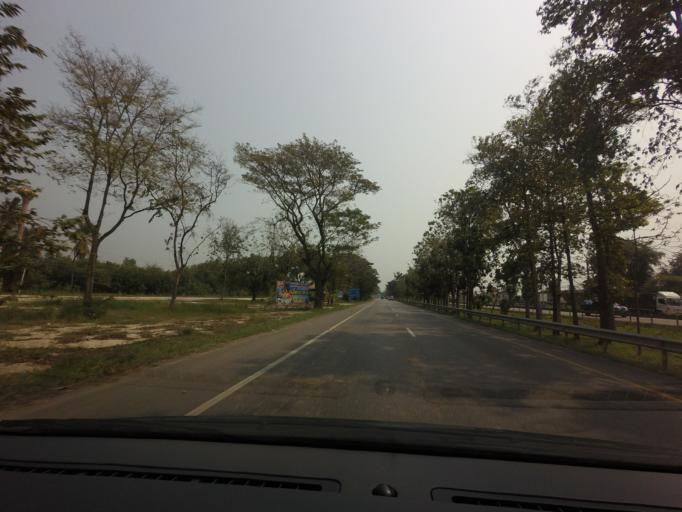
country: TH
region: Prachuap Khiri Khan
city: Pran Buri
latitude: 12.4255
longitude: 99.9201
